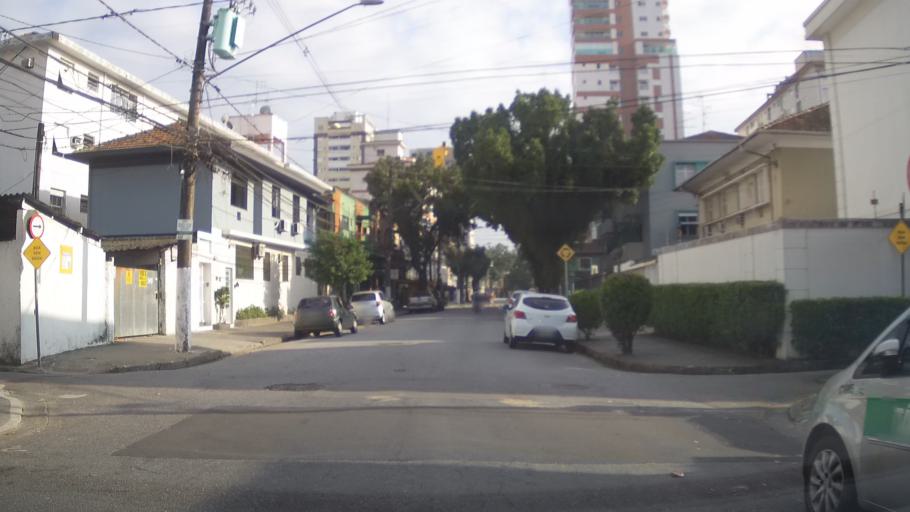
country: BR
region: Sao Paulo
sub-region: Santos
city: Santos
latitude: -23.9603
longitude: -46.3249
